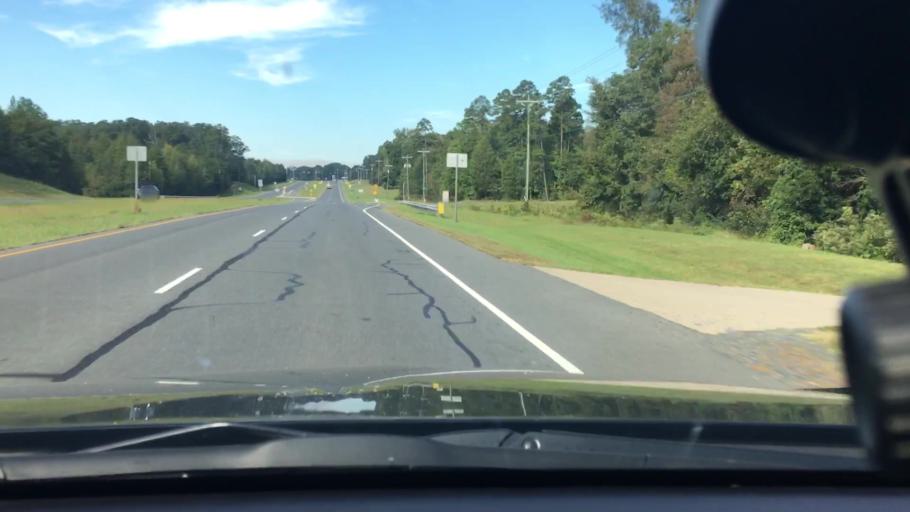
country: US
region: North Carolina
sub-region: Stanly County
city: Oakboro
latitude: 35.2691
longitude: -80.3379
